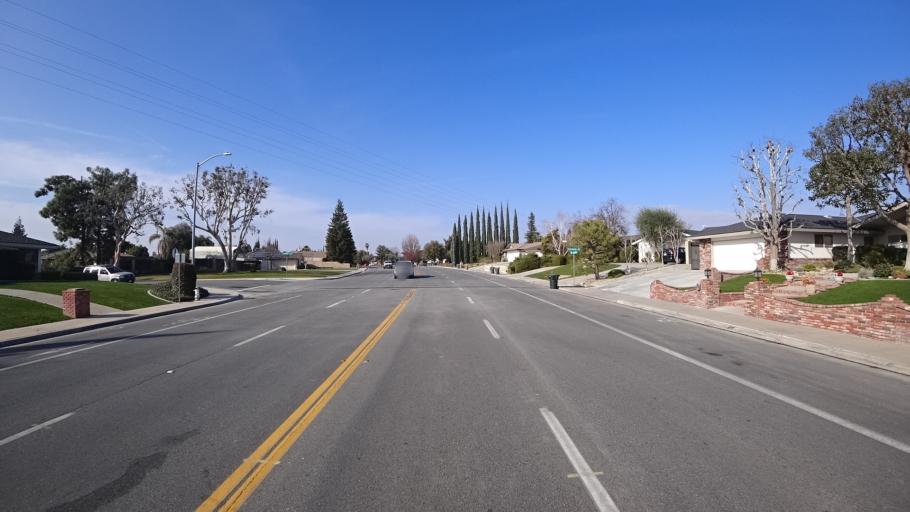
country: US
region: California
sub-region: Kern County
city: Oildale
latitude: 35.4086
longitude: -118.9396
